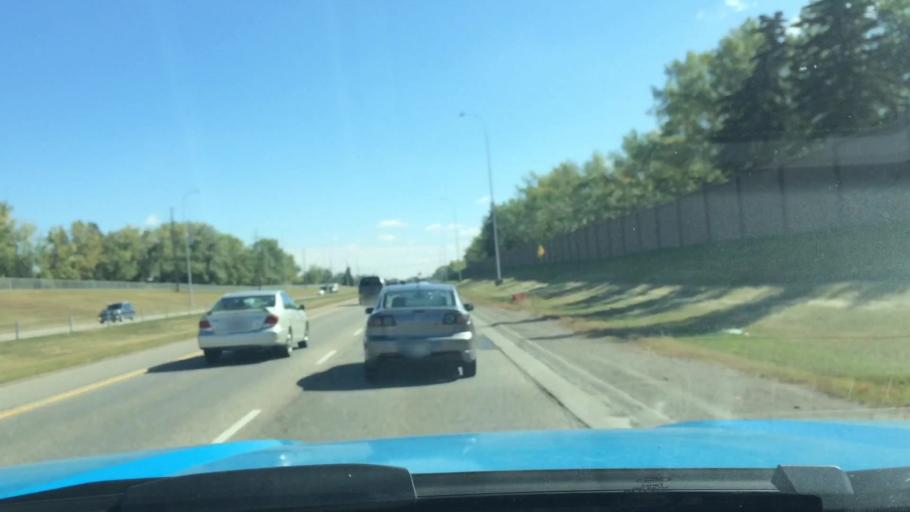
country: CA
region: Alberta
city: Calgary
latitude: 50.9481
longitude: -114.0526
